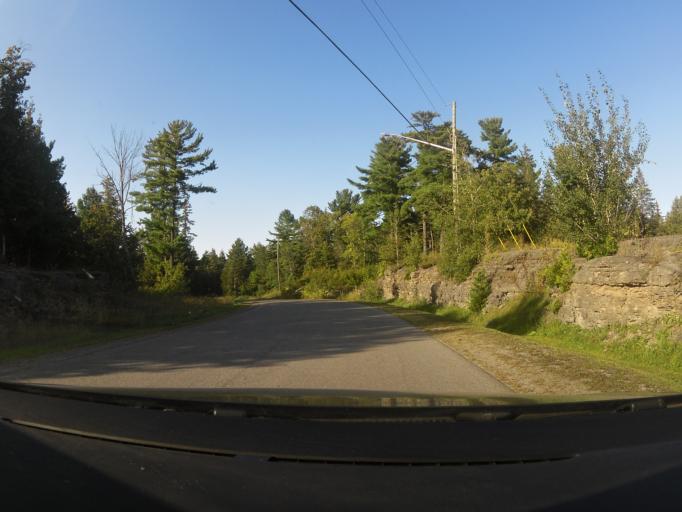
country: CA
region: Ontario
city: Carleton Place
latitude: 45.2908
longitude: -76.1111
